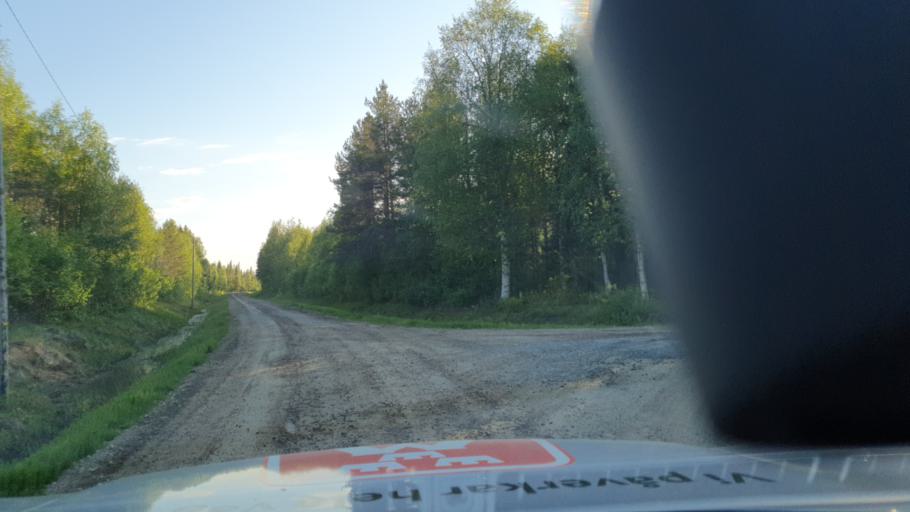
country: FI
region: Lapland
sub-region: Torniolaakso
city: Ylitornio
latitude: 66.1554
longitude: 23.6473
